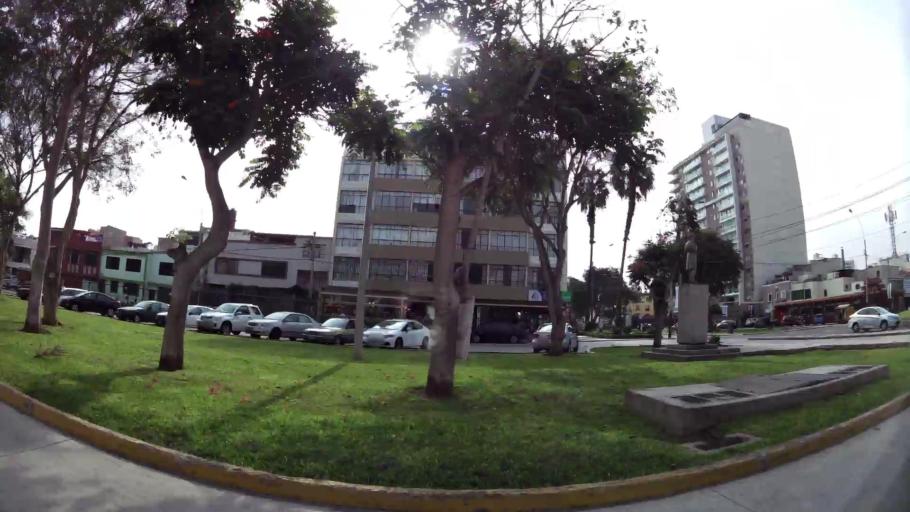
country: PE
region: Lima
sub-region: Lima
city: San Isidro
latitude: -12.0916
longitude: -77.0643
